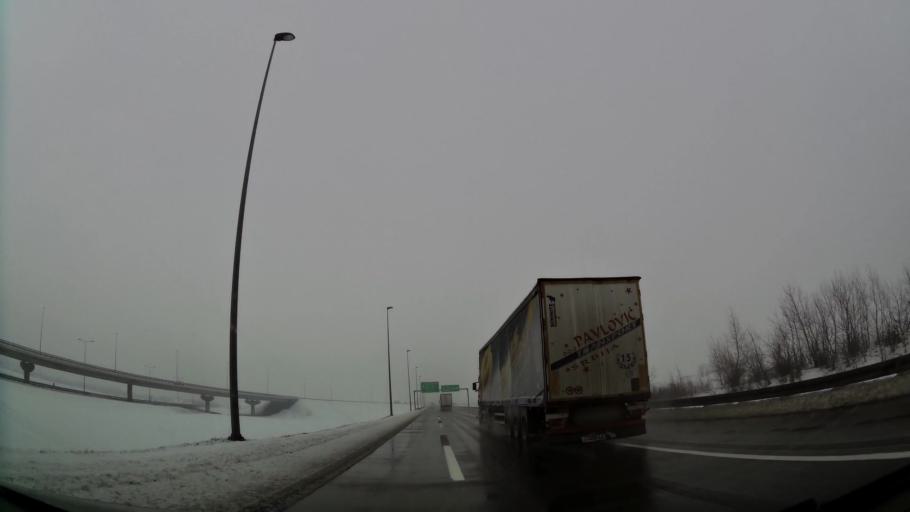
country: RS
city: Dobanovci
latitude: 44.8288
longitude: 20.2516
